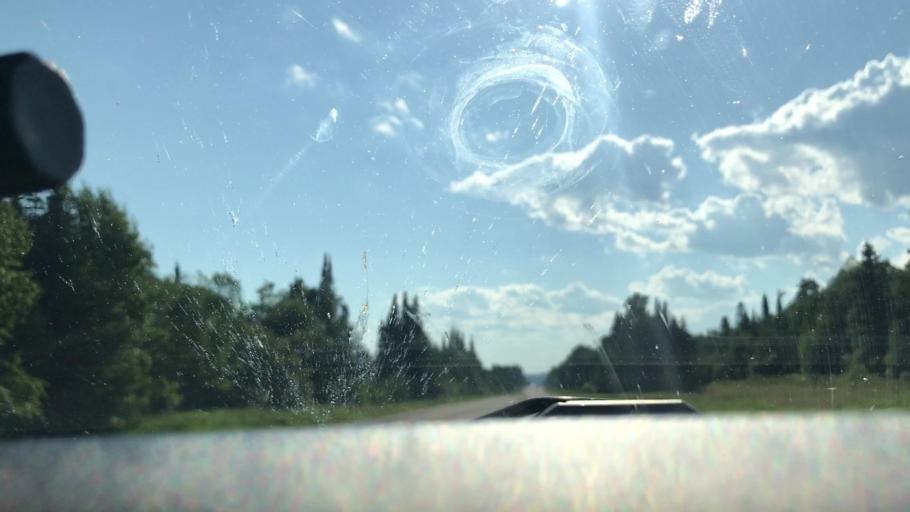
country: US
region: Minnesota
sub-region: Cook County
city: Grand Marais
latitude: 47.7972
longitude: -90.1146
